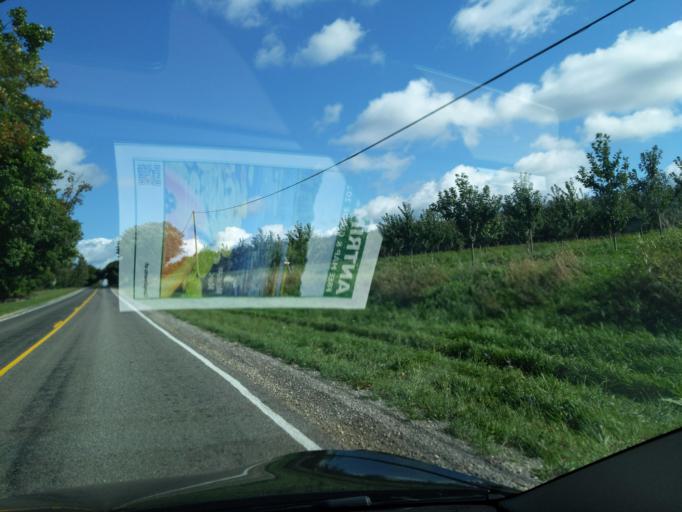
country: US
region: Michigan
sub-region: Antrim County
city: Elk Rapids
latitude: 44.9386
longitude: -85.3592
